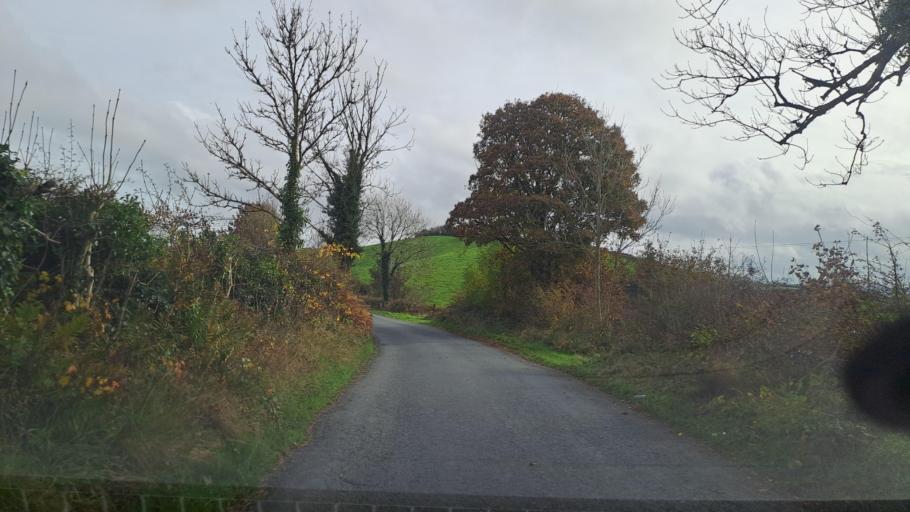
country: IE
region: Ulster
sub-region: An Cabhan
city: Bailieborough
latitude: 54.0219
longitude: -6.9199
